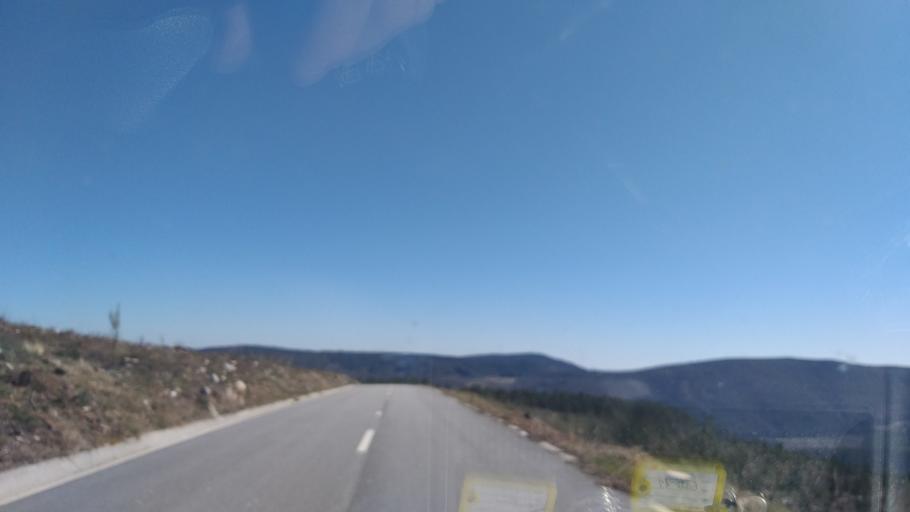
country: PT
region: Guarda
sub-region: Manteigas
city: Manteigas
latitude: 40.4791
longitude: -7.5113
